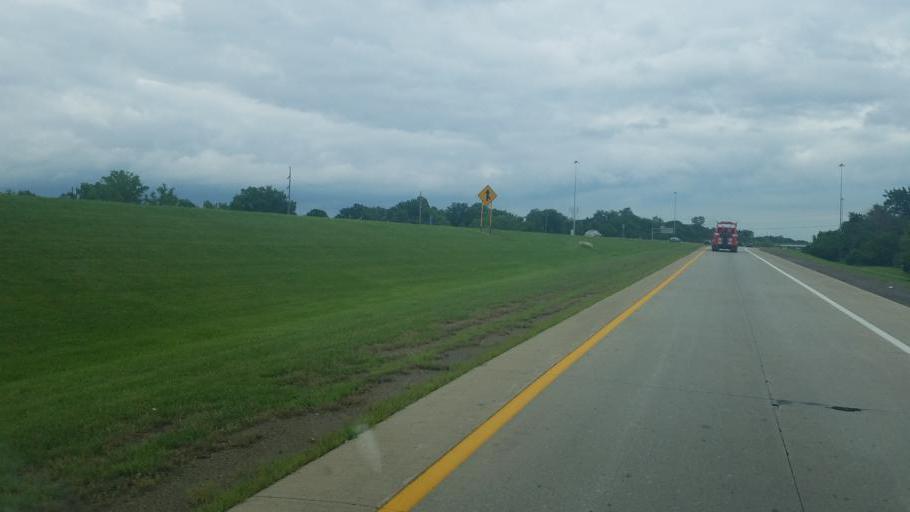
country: US
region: Ohio
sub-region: Franklin County
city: Grove City
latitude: 39.9028
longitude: -83.0747
